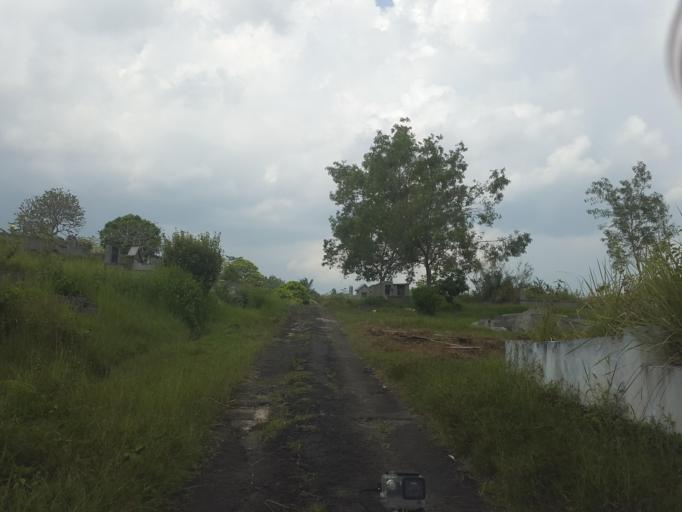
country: ID
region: Central Java
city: Purwokerto
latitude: -7.4542
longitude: 109.2235
